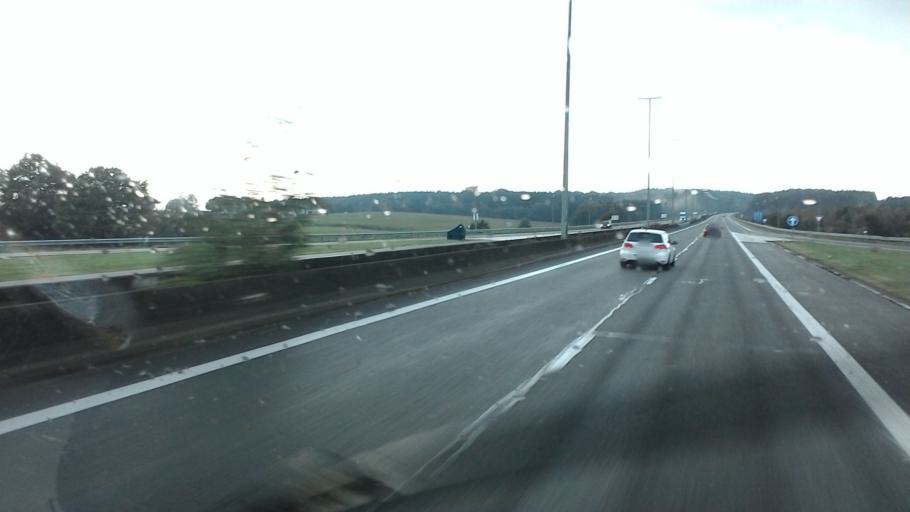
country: BE
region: Wallonia
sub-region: Province du Luxembourg
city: Houffalize
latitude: 50.1746
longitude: 5.7888
